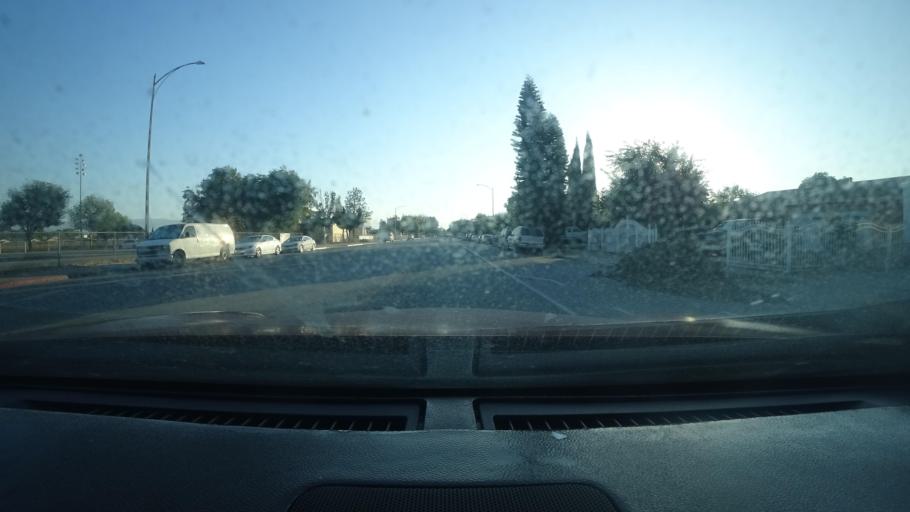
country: US
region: California
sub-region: Santa Clara County
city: Alum Rock
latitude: 37.3432
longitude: -121.8132
